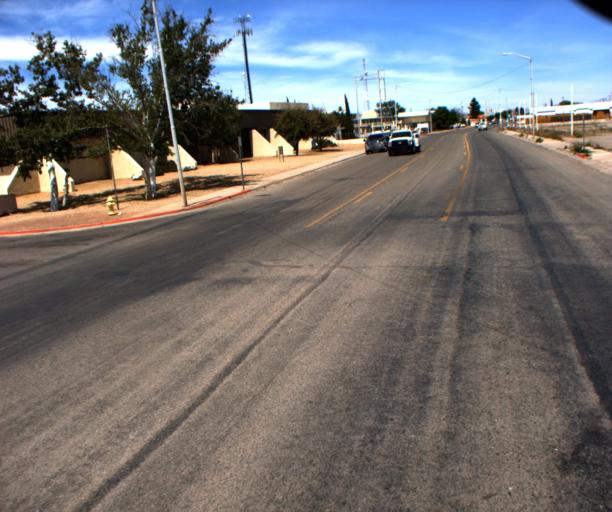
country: US
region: Arizona
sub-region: Cochise County
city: Willcox
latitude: 32.2481
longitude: -109.8352
